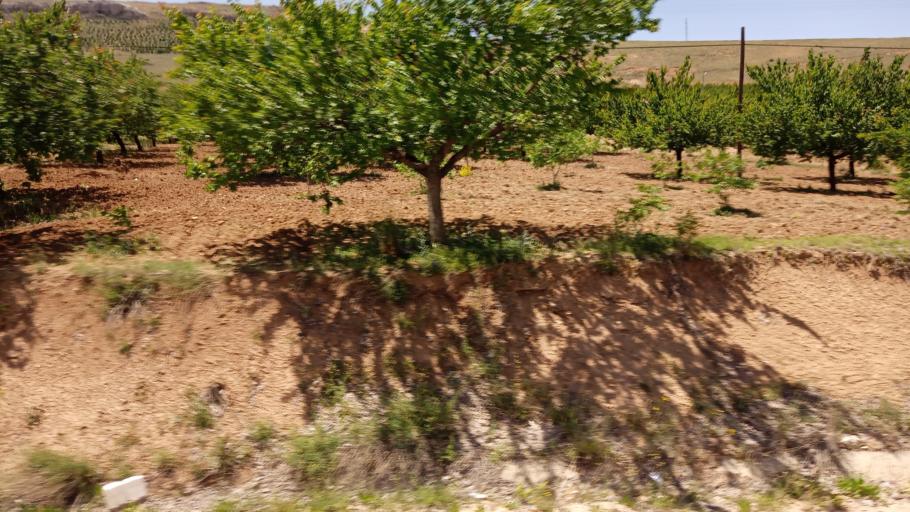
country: TR
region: Malatya
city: Darende
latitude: 38.6157
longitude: 37.4552
